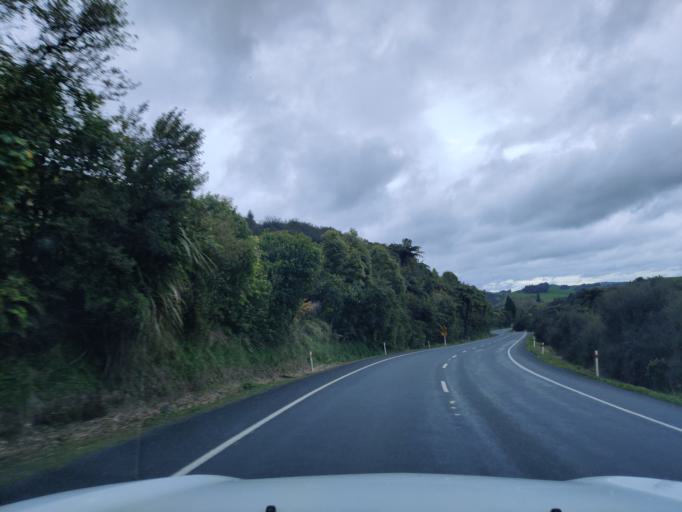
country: NZ
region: Waikato
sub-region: Otorohanga District
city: Otorohanga
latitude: -38.5089
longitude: 175.2052
